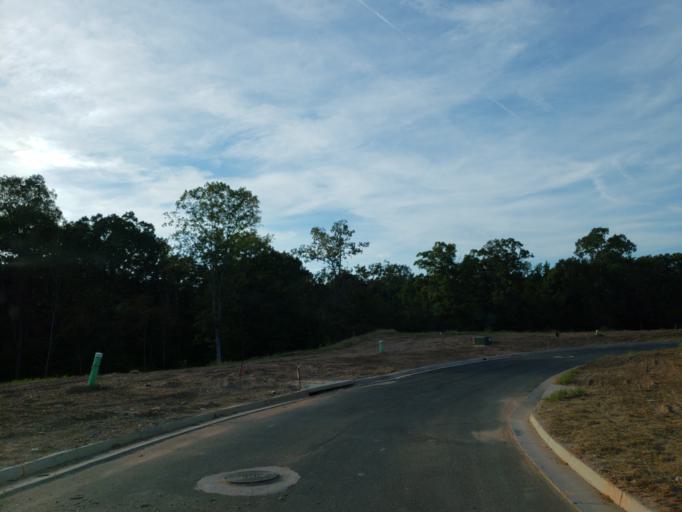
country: US
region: Georgia
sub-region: Fulton County
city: Roswell
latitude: 34.0559
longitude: -84.4361
